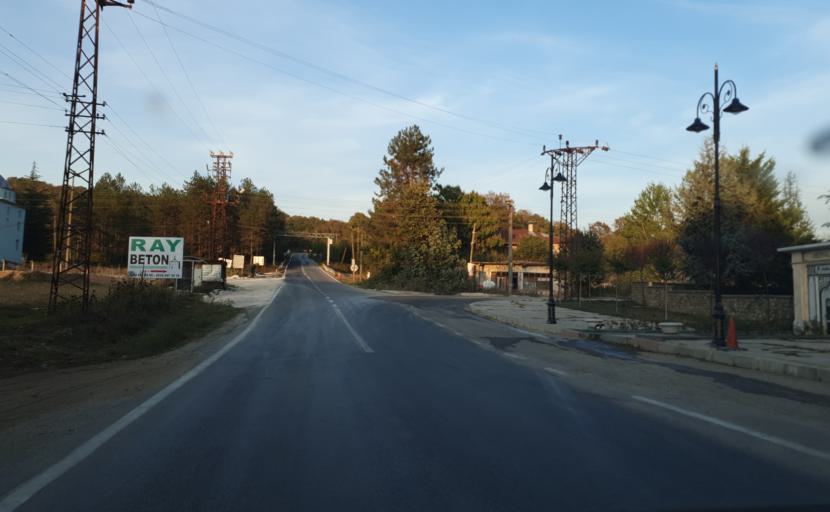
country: TR
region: Kirklareli
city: Sergen
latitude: 41.8343
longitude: 27.7913
